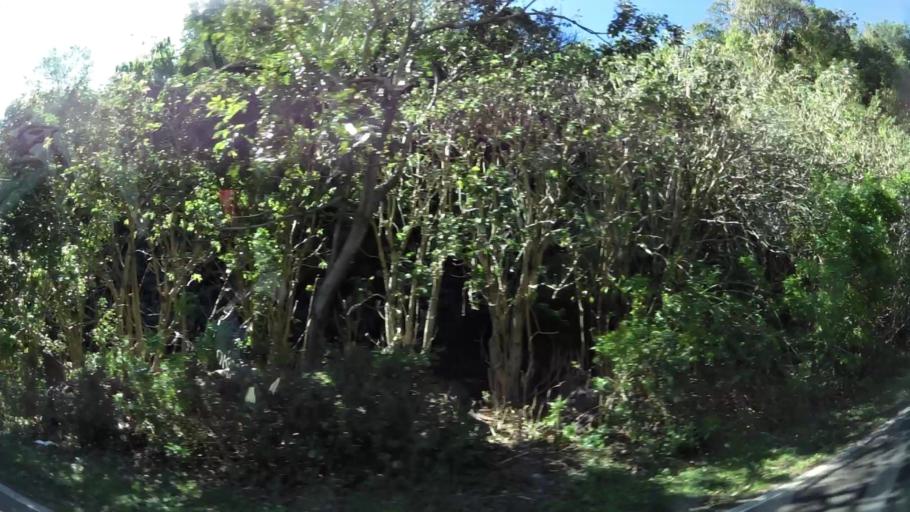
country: SV
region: Sonsonate
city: Juayua
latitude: 13.8483
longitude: -89.7671
